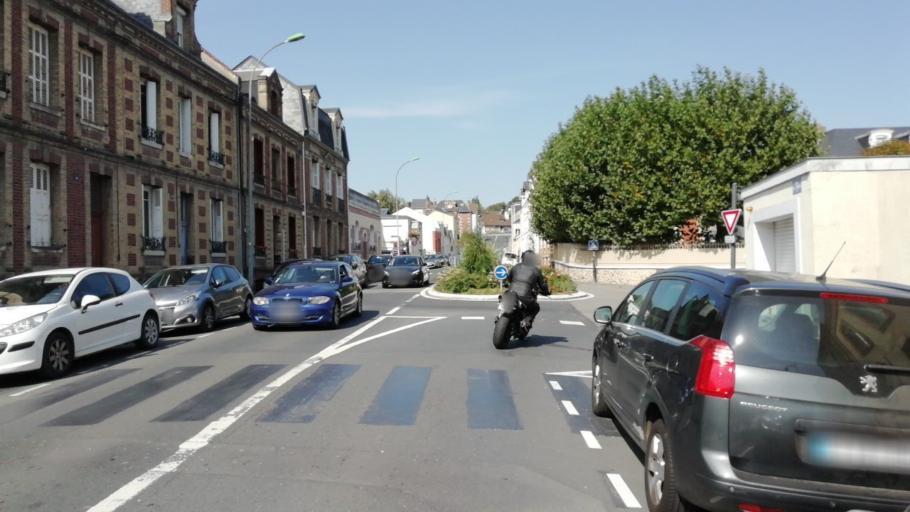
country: FR
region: Haute-Normandie
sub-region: Departement de la Seine-Maritime
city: Montivilliers
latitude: 49.5439
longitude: 0.1895
